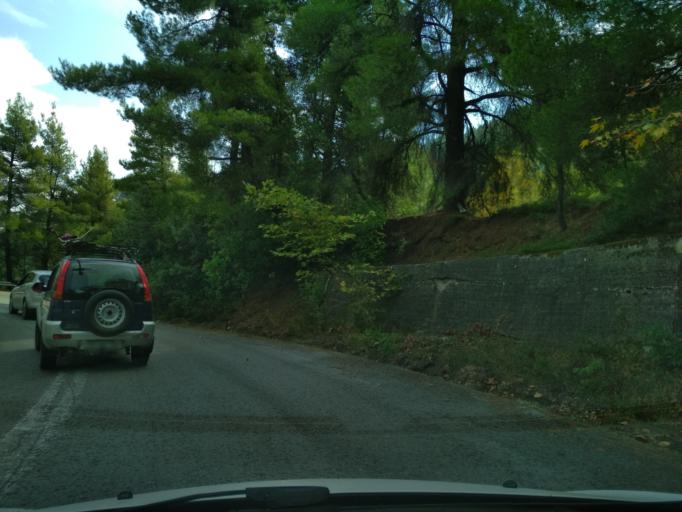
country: GR
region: Central Greece
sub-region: Nomos Evvoias
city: Politika
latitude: 38.6714
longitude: 23.5589
